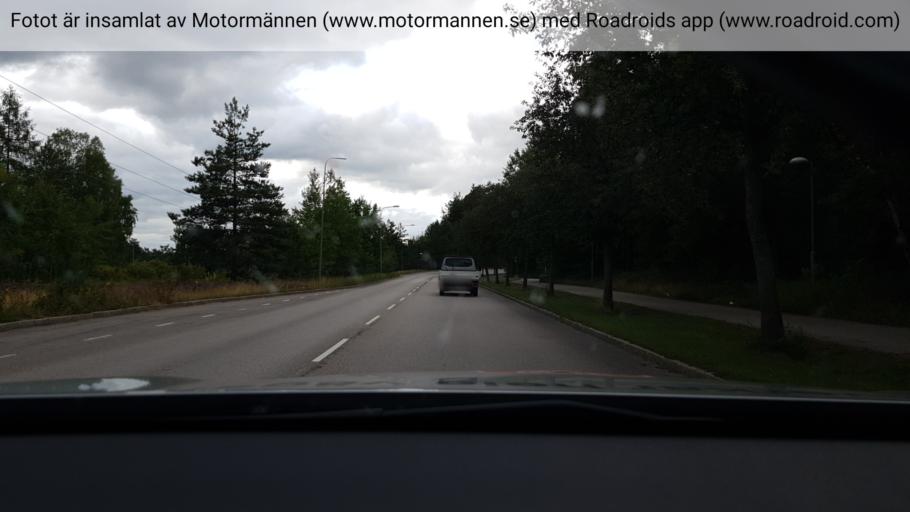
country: SE
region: Stockholm
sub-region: Nacka Kommun
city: Alta
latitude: 59.2356
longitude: 18.1944
